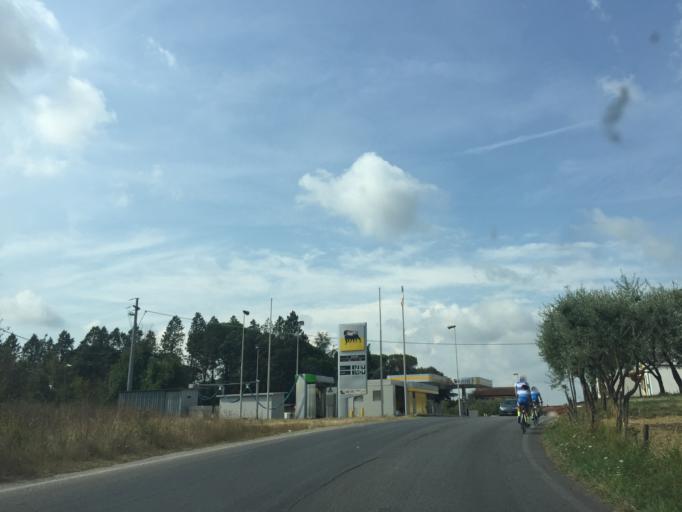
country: IT
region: Tuscany
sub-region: Provincia di Pistoia
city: Lamporecchio
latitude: 43.8072
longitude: 10.8868
